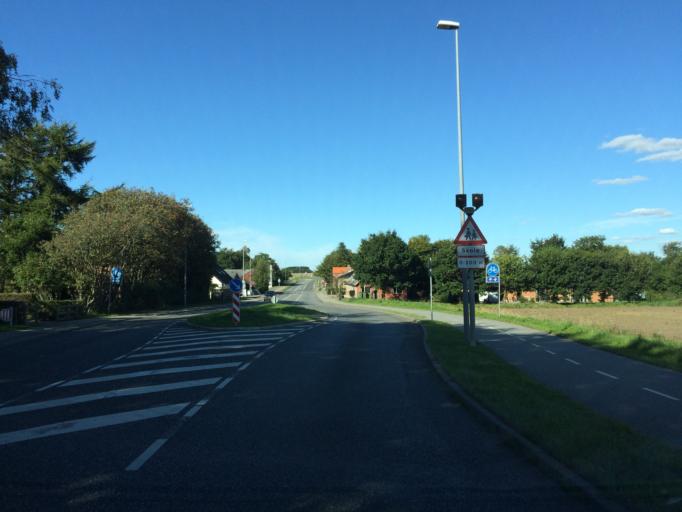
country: DK
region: Central Jutland
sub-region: Holstebro Kommune
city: Holstebro
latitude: 56.3138
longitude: 8.6057
